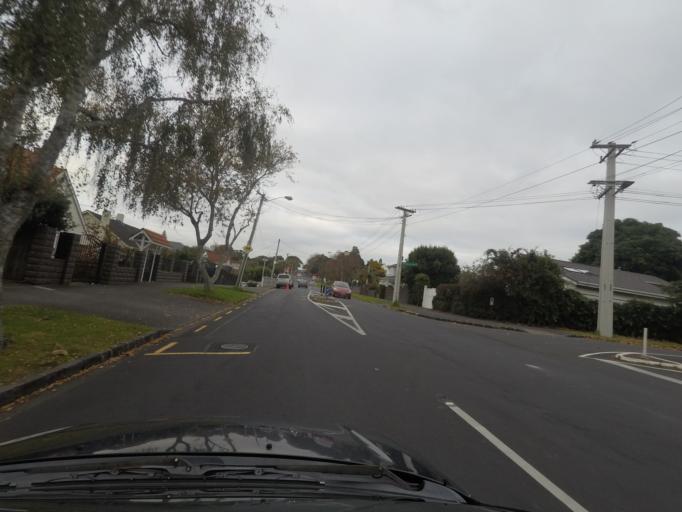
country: NZ
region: Auckland
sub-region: Auckland
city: Auckland
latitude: -36.8893
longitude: 174.7667
